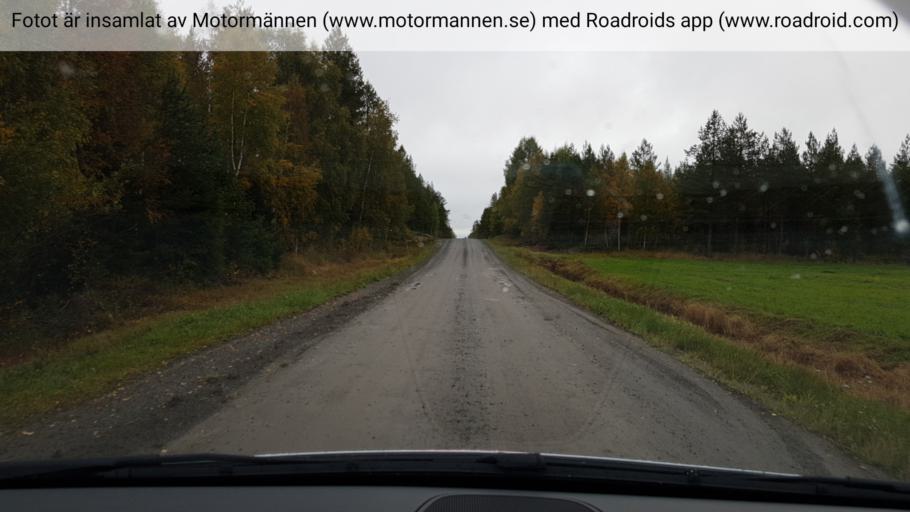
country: SE
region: Vaesterbotten
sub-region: Umea Kommun
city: Ersmark
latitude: 64.1022
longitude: 20.2674
